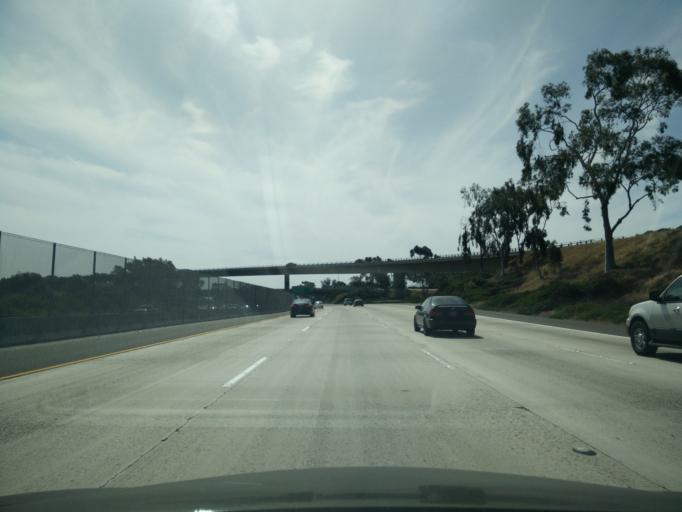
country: US
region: California
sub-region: San Diego County
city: Imperial Beach
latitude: 32.5676
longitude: -117.0756
